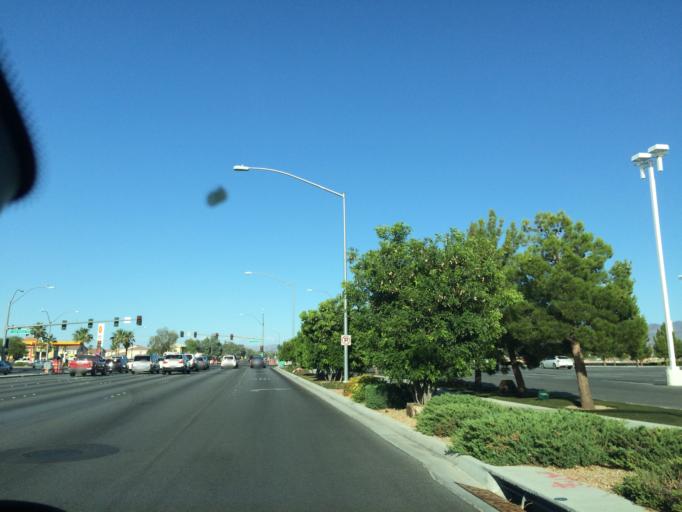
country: US
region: Nevada
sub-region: Clark County
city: Enterprise
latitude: 36.0136
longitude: -115.1737
